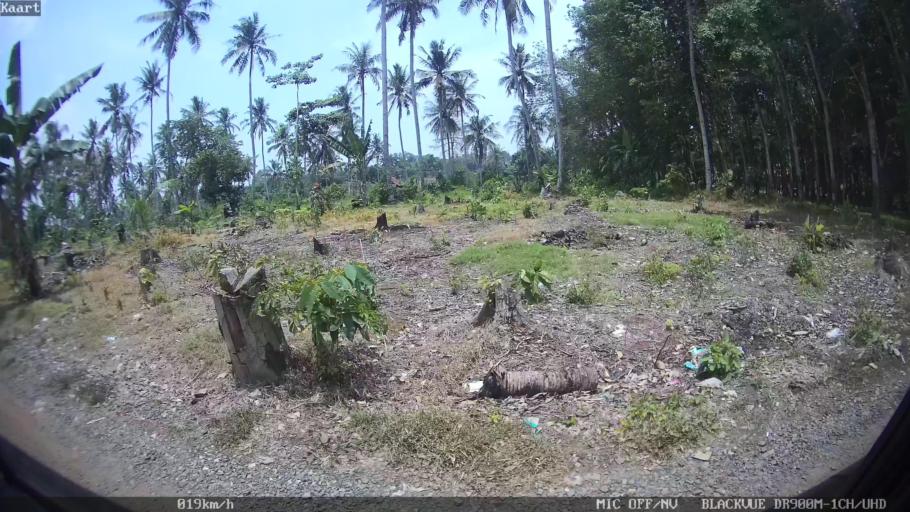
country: ID
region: Lampung
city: Natar
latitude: -5.3154
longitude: 105.2459
